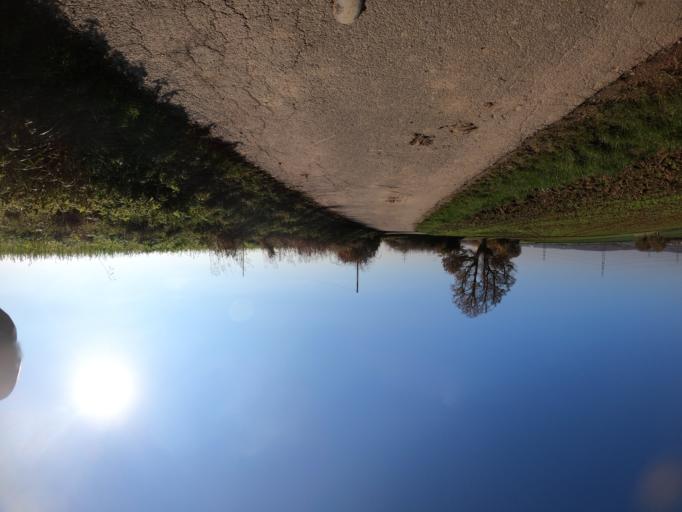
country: DE
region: Baden-Wuerttemberg
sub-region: Regierungsbezirk Stuttgart
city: Magstadt
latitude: 48.7299
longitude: 8.9440
